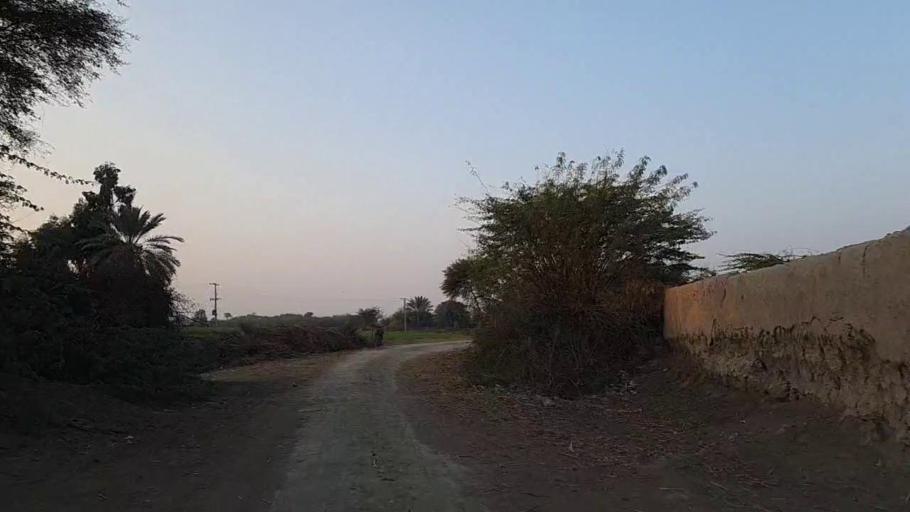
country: PK
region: Sindh
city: Jam Sahib
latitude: 26.3077
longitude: 68.5779
